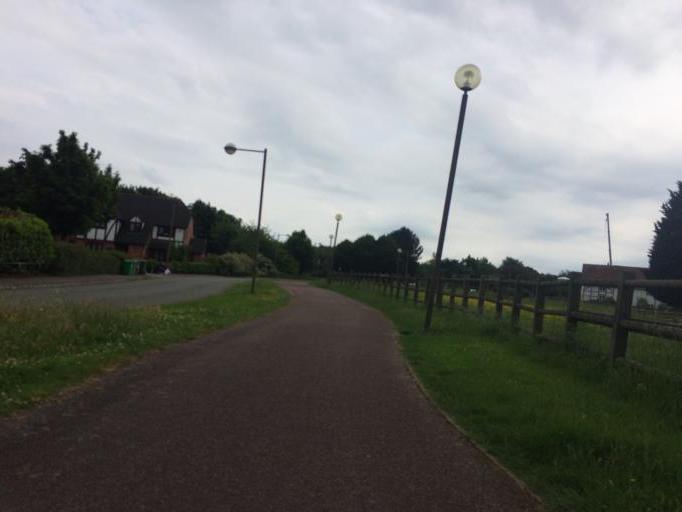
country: GB
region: England
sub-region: Milton Keynes
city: Loughton
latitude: 52.0293
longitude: -0.7750
